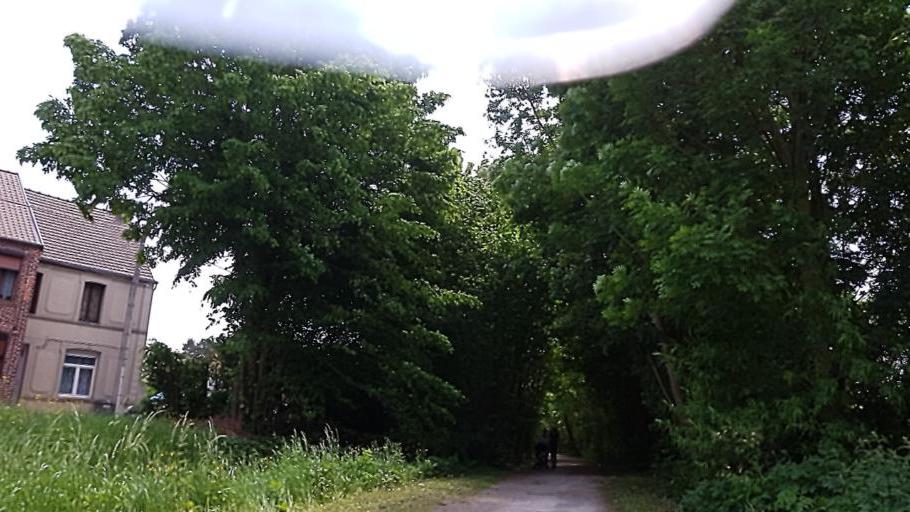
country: FR
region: Nord-Pas-de-Calais
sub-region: Departement du Nord
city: Vieux-Conde
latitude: 50.4677
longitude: 3.5734
